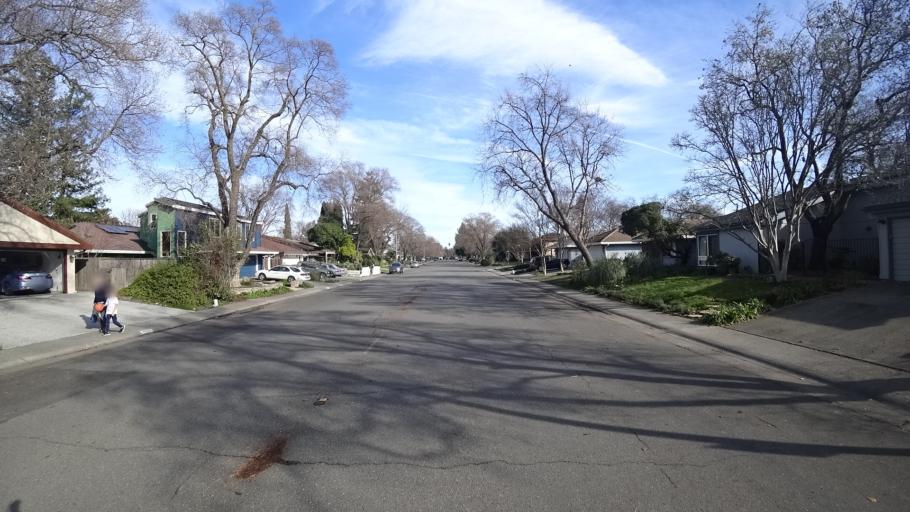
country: US
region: California
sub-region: Yolo County
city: Davis
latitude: 38.5464
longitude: -121.7027
